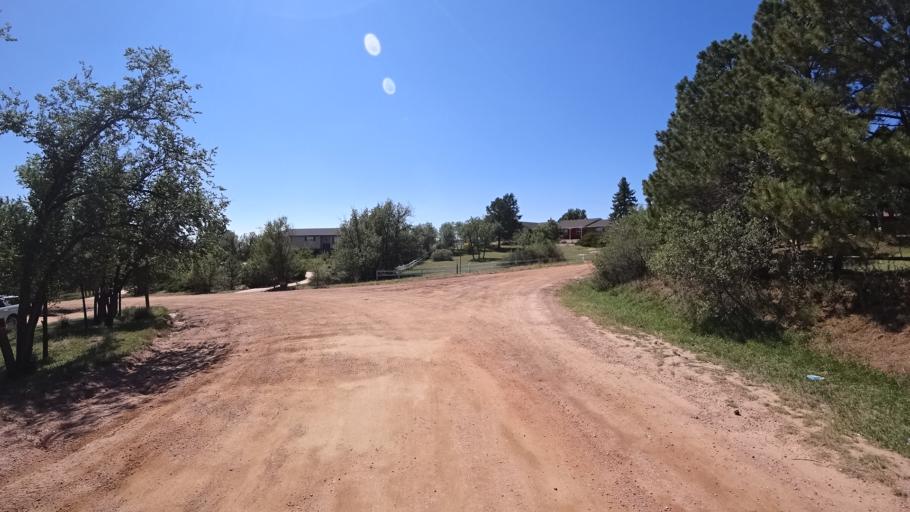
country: US
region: Colorado
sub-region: El Paso County
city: Cimarron Hills
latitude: 38.8647
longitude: -104.7385
